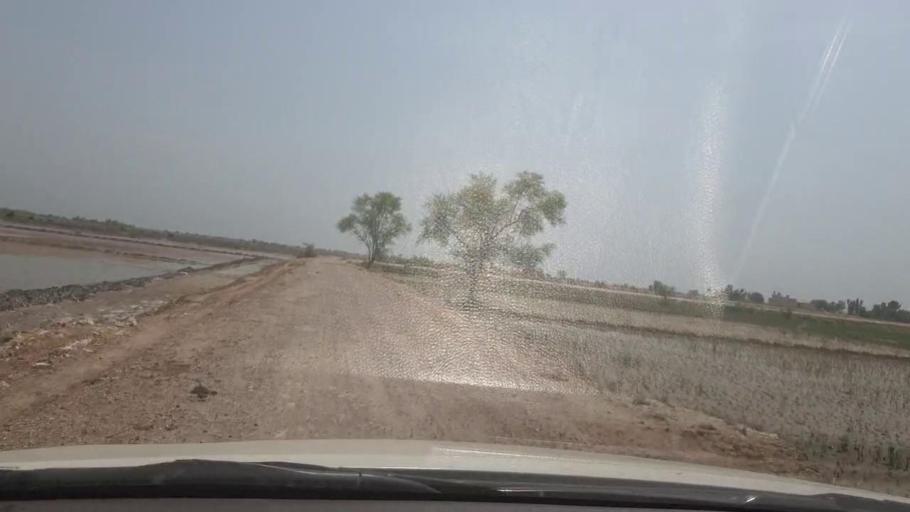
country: PK
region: Sindh
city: Shikarpur
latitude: 28.0379
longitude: 68.5737
